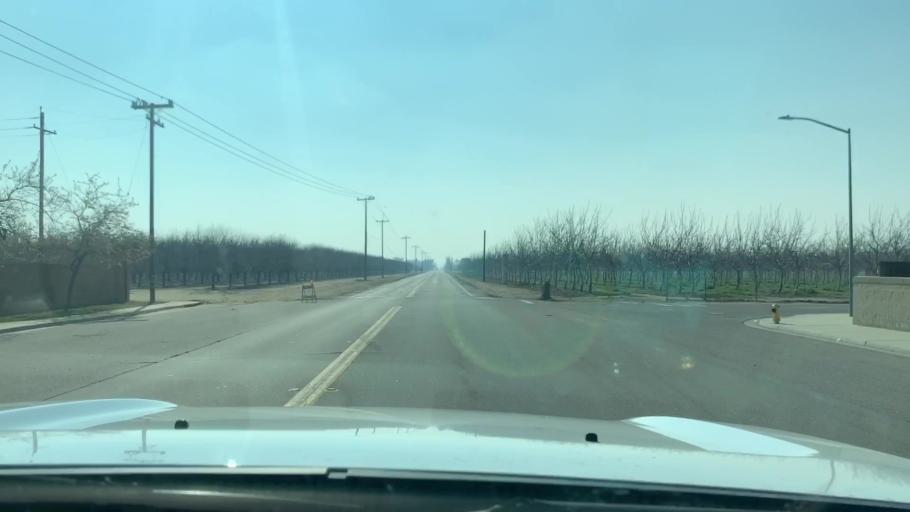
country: US
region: California
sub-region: Kern County
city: Shafter
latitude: 35.4893
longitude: -119.2785
